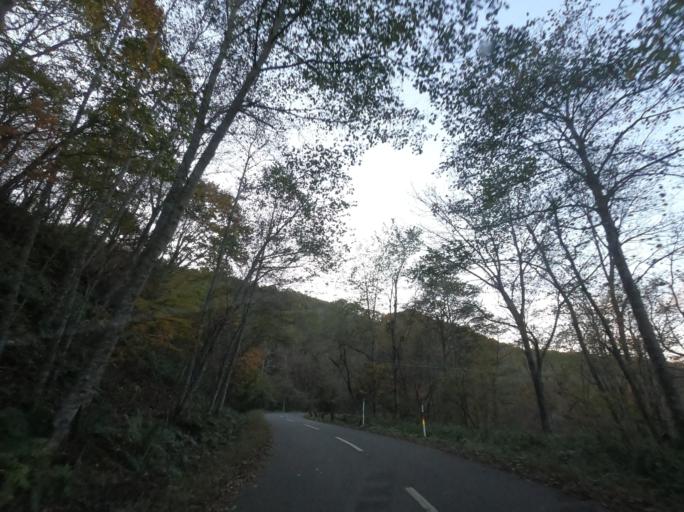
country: JP
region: Hokkaido
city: Kushiro
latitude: 43.1999
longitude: 144.4588
